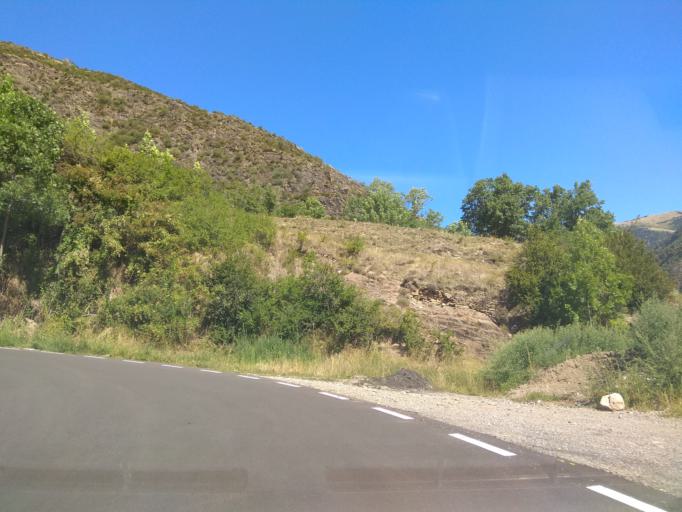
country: ES
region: Catalonia
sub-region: Provincia de Lleida
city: Vielha
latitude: 42.5261
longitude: 0.8283
